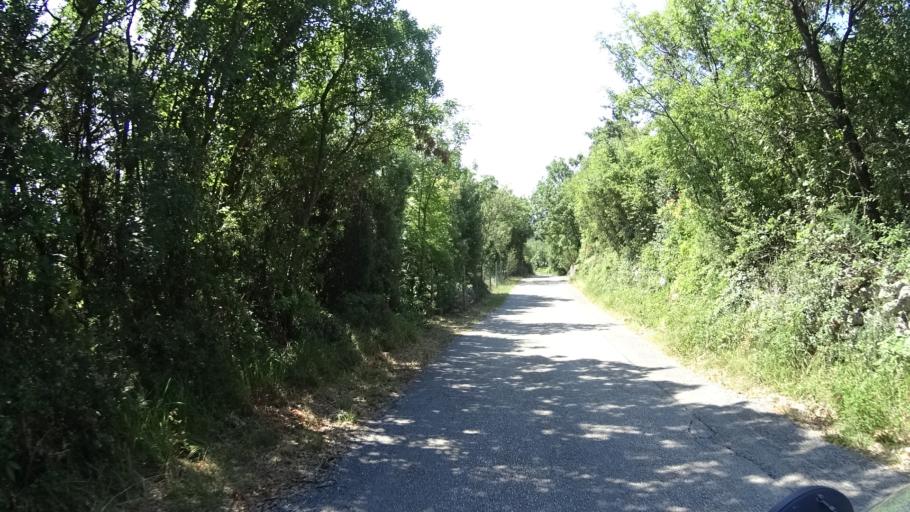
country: HR
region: Istarska
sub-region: Grad Labin
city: Rabac
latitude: 44.9892
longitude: 14.1568
